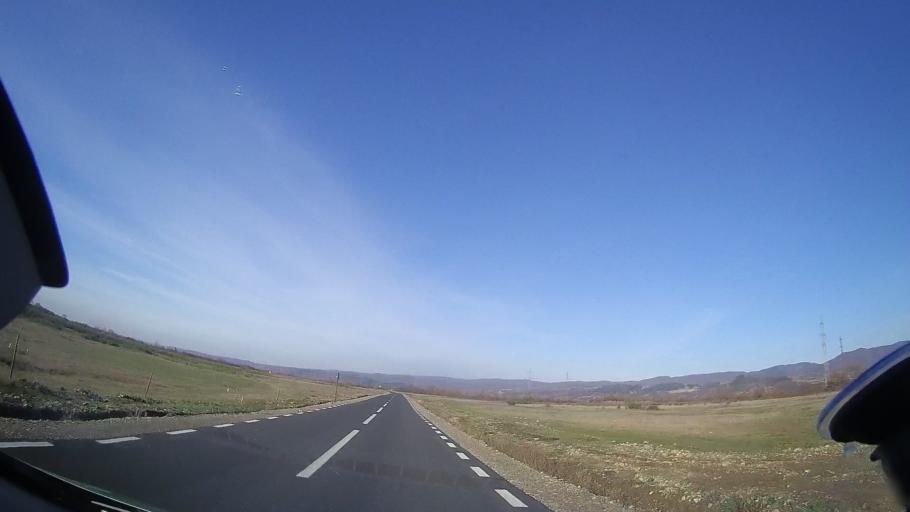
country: RO
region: Bihor
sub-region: Comuna Auseu
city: Auseu
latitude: 47.0088
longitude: 22.5025
